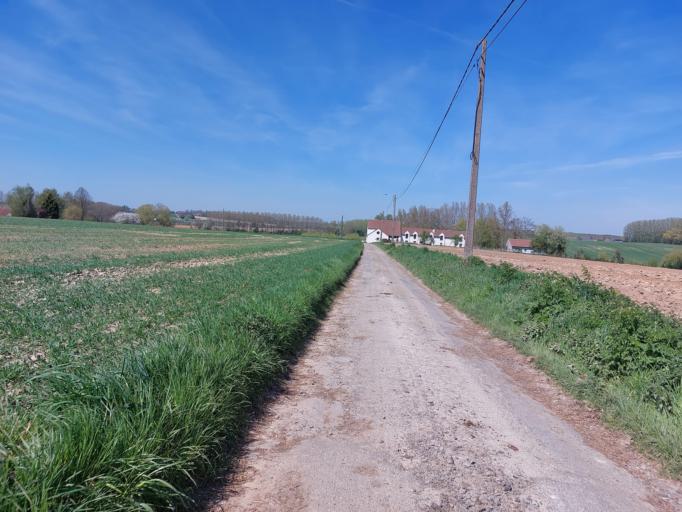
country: BE
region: Wallonia
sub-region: Province du Hainaut
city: Silly
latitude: 50.5988
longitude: 3.9772
